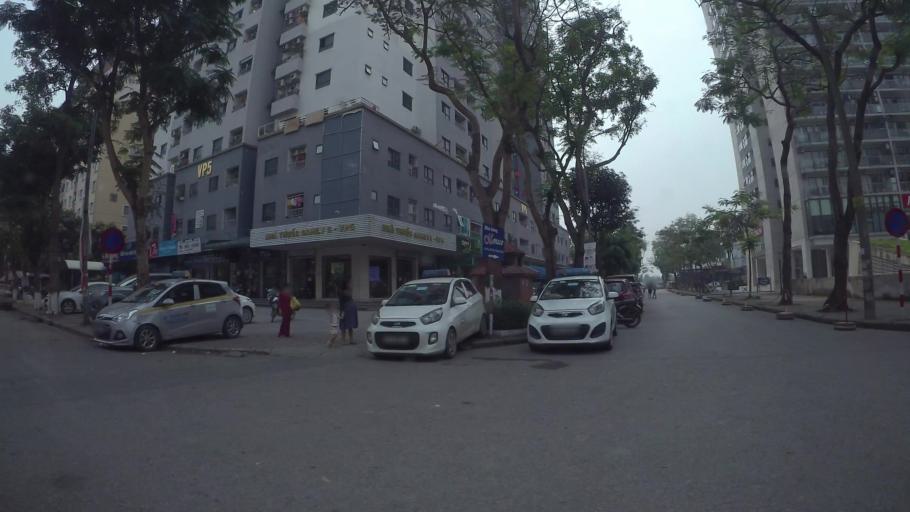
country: VN
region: Ha Noi
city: Van Dien
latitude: 20.9638
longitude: 105.8313
